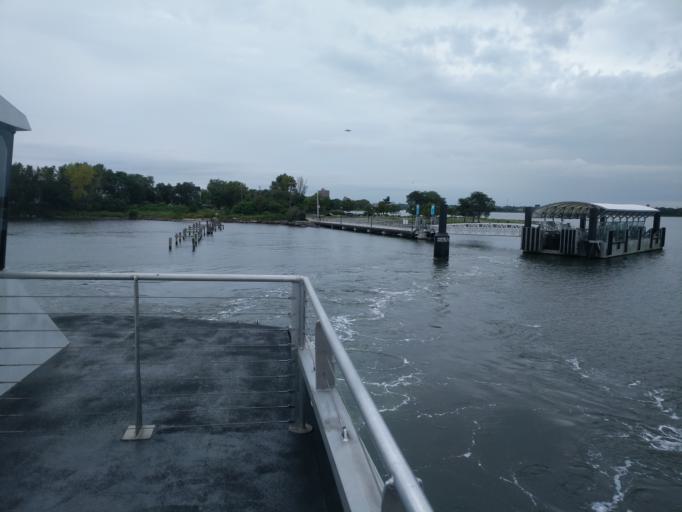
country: US
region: New York
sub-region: Bronx
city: The Bronx
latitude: 40.8036
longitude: -73.8494
